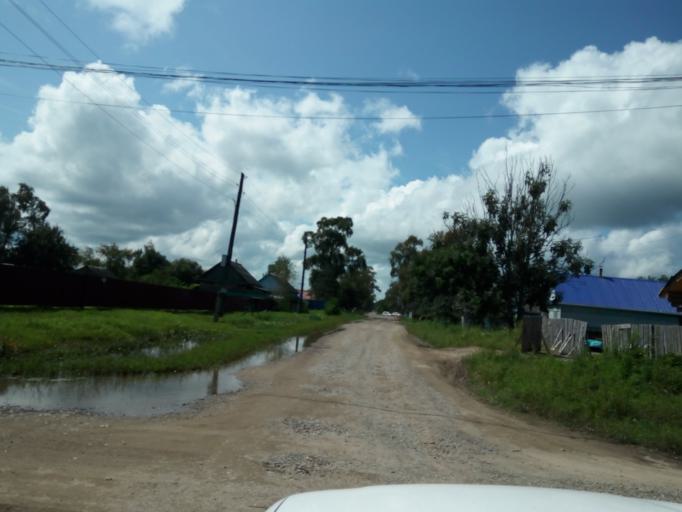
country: RU
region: Primorskiy
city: Dal'nerechensk
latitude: 45.9255
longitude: 133.7433
